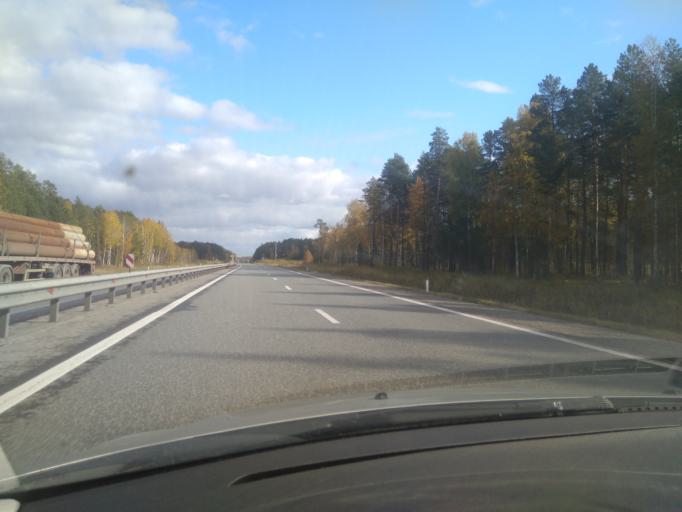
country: RU
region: Sverdlovsk
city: Lugovskoy
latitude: 57.0762
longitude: 64.5196
